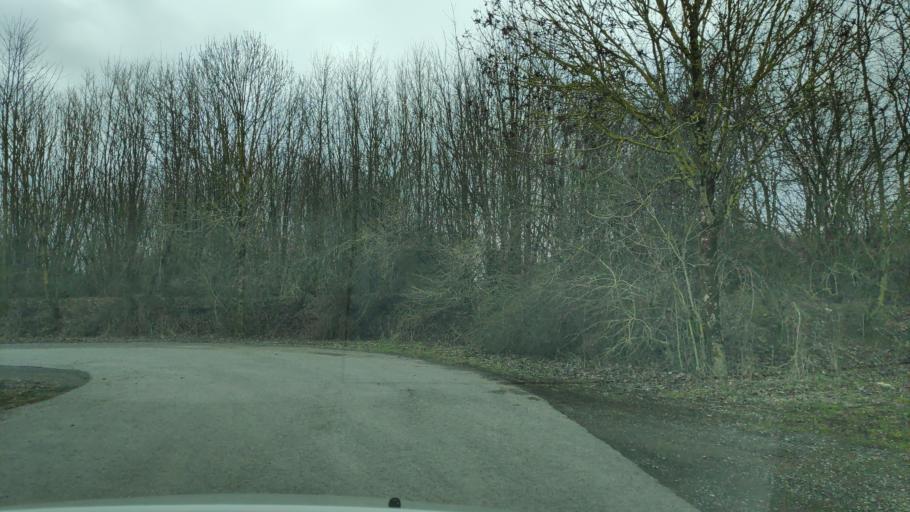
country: DE
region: Lower Saxony
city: Hessisch Oldendorf
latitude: 52.2061
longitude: 9.2861
